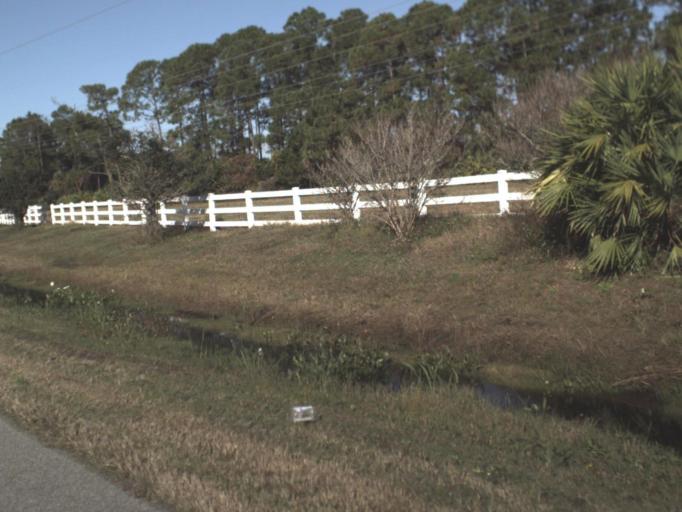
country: US
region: Florida
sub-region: Volusia County
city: Holly Hill
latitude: 29.2150
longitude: -81.0774
